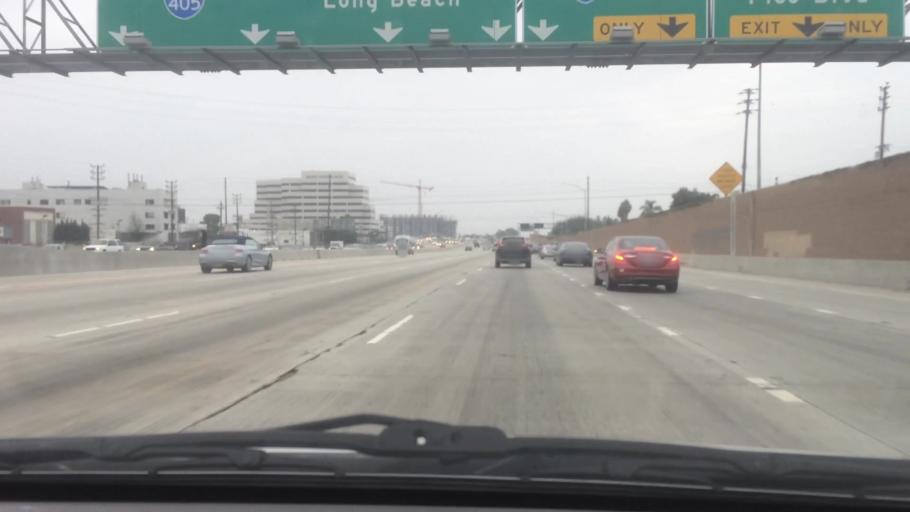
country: US
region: California
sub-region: Los Angeles County
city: Westwood, Los Angeles
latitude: 34.0425
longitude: -118.4431
